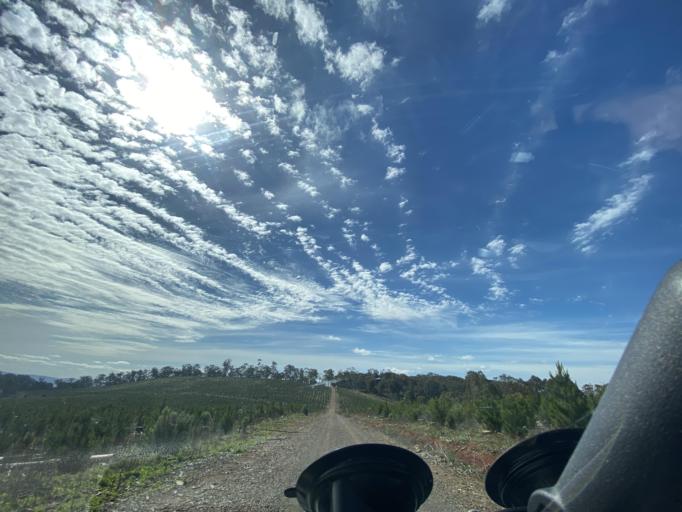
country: AU
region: Victoria
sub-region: Mansfield
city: Mansfield
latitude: -36.8220
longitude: 146.1031
